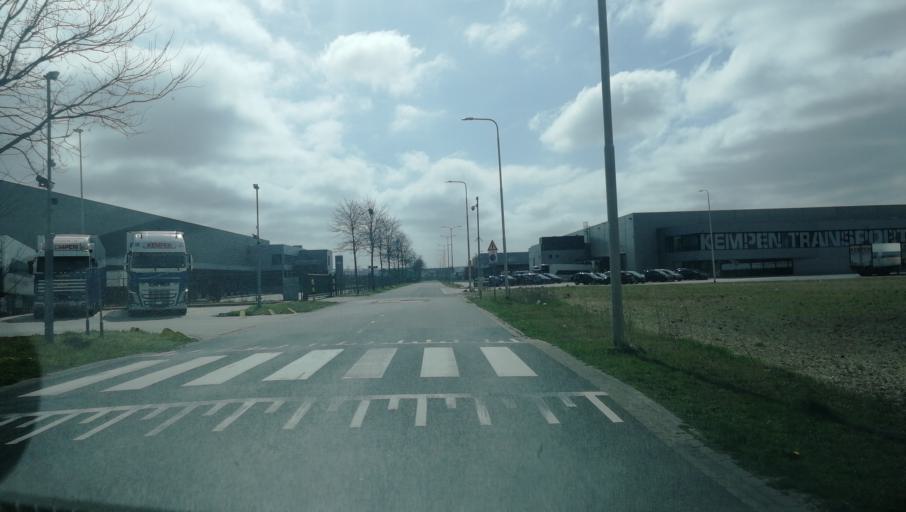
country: NL
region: Limburg
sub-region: Gemeente Venlo
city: Venlo
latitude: 51.4133
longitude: 6.1326
